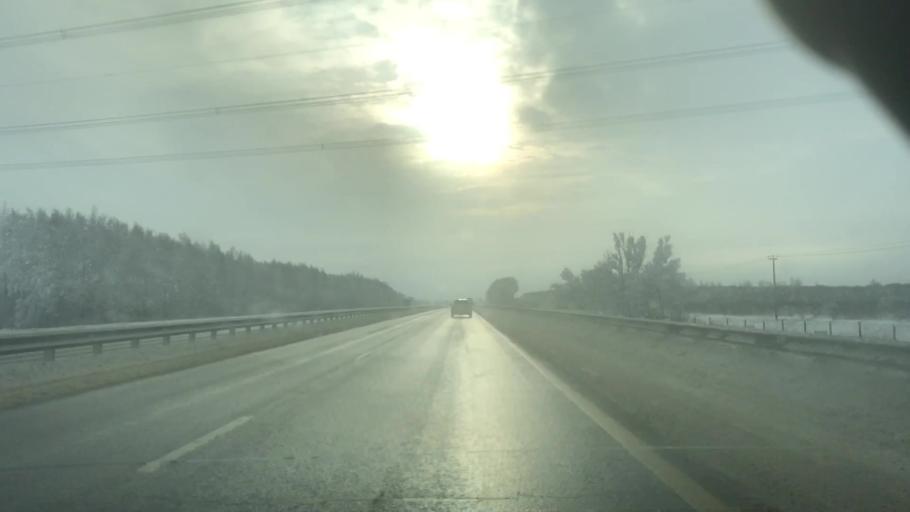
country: RU
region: Tula
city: Venev
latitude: 54.2898
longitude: 38.1594
